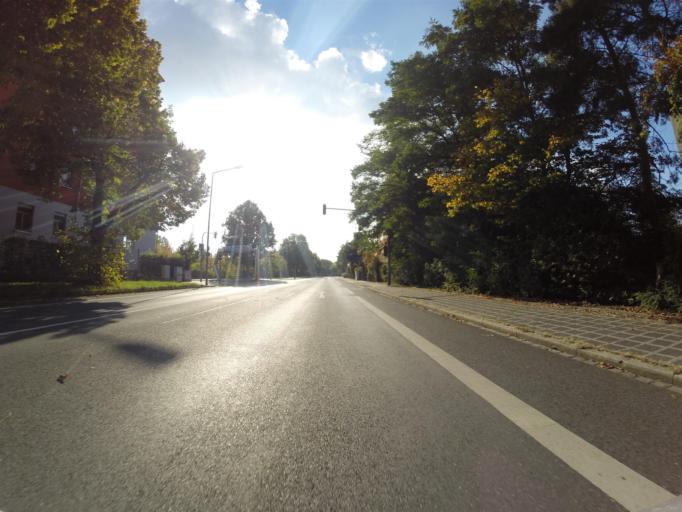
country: DE
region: Bavaria
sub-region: Regierungsbezirk Mittelfranken
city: Grossreuth bei Schweinau
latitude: 49.4377
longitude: 11.0320
